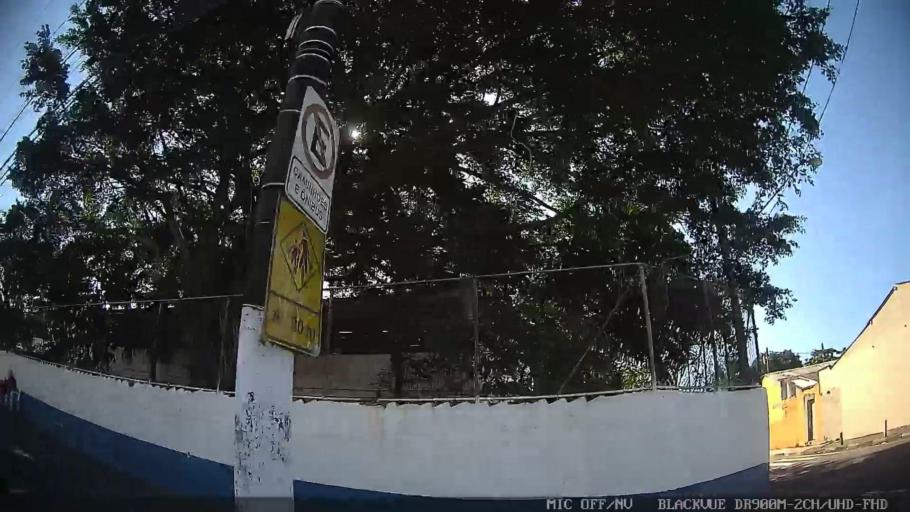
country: BR
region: Sao Paulo
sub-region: Santos
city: Santos
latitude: -23.9543
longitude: -46.2881
